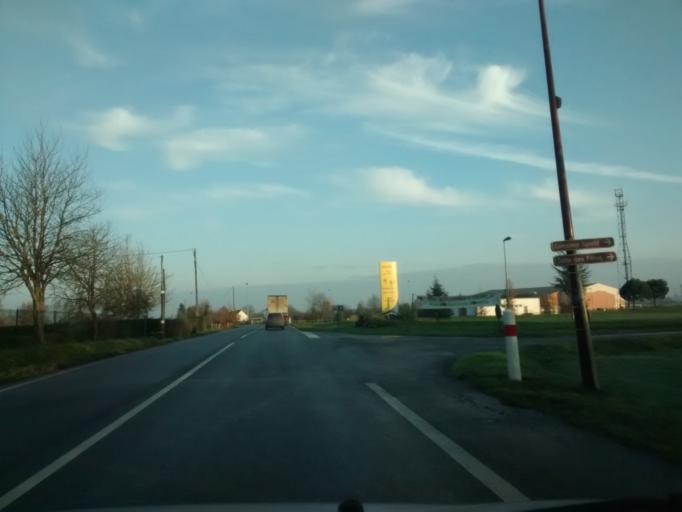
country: FR
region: Brittany
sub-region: Departement d'Ille-et-Vilaine
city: Tremblay
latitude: 48.4276
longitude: -1.4729
